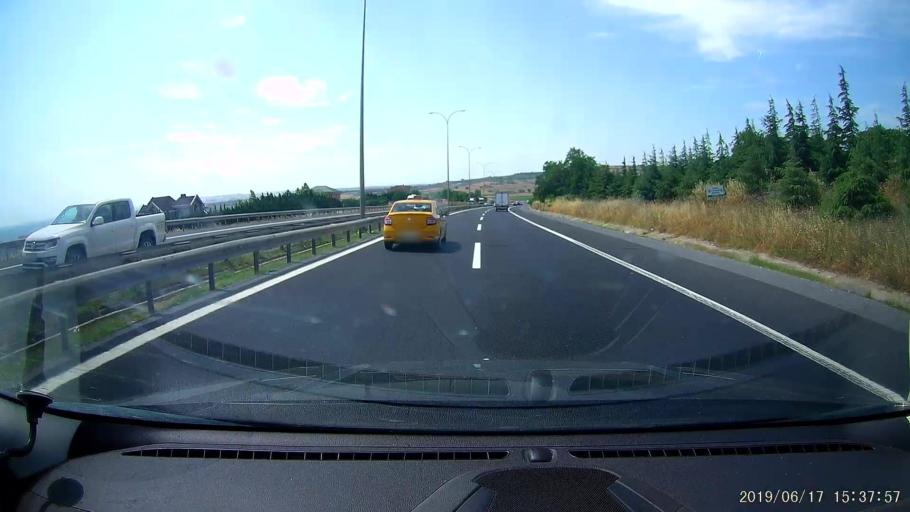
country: TR
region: Istanbul
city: Celaliye
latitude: 41.0598
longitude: 28.4117
